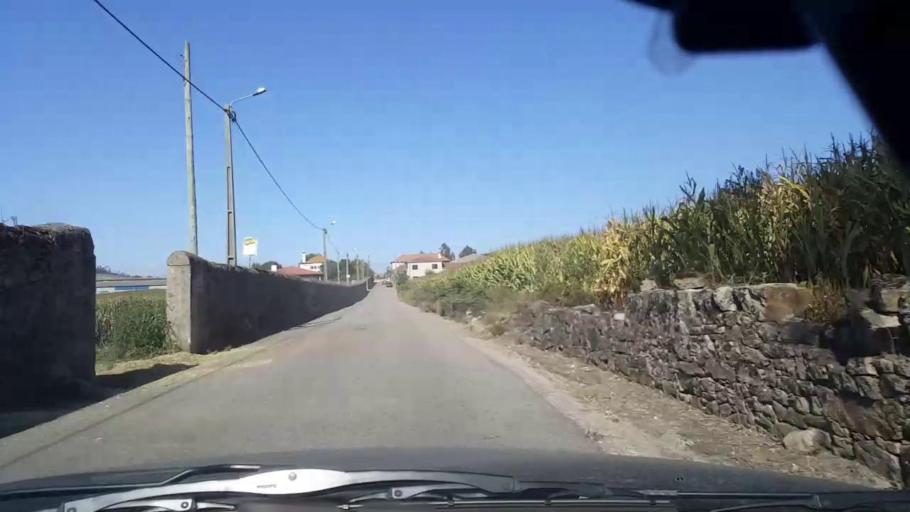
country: PT
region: Porto
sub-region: Vila do Conde
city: Arvore
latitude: 41.3669
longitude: -8.6466
